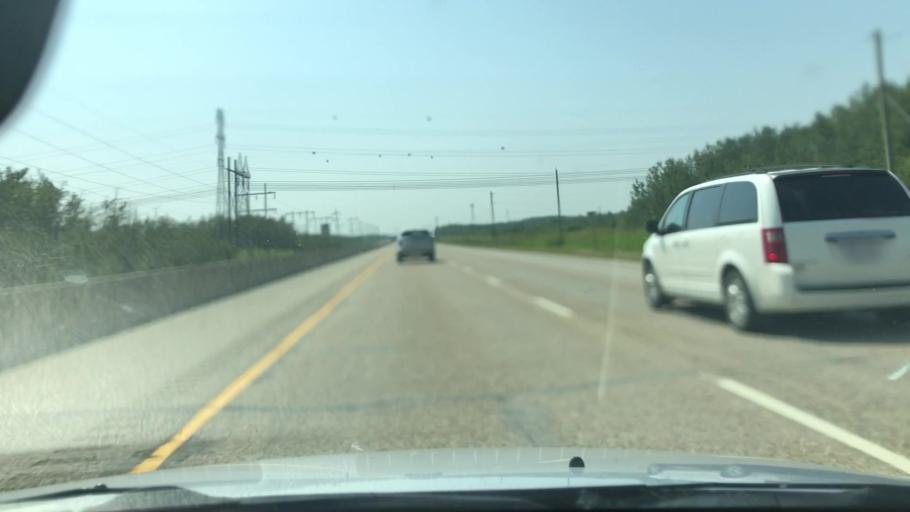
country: CA
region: Alberta
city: Devon
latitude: 53.4635
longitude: -113.7626
